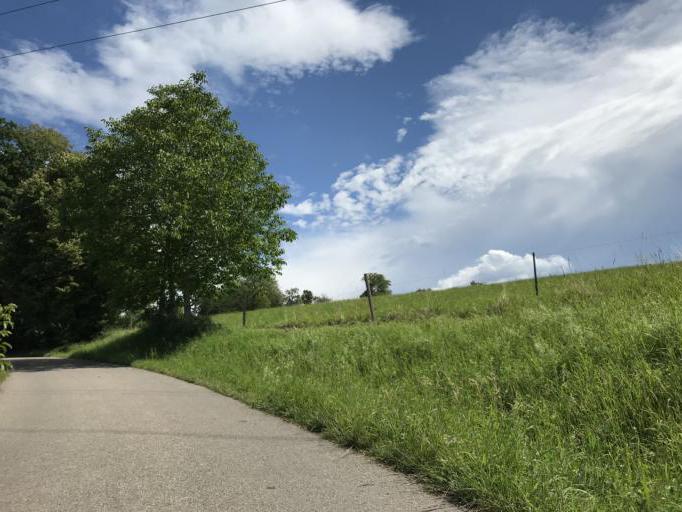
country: DE
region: Baden-Wuerttemberg
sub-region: Freiburg Region
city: Schopfheim
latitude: 47.6404
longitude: 7.8283
